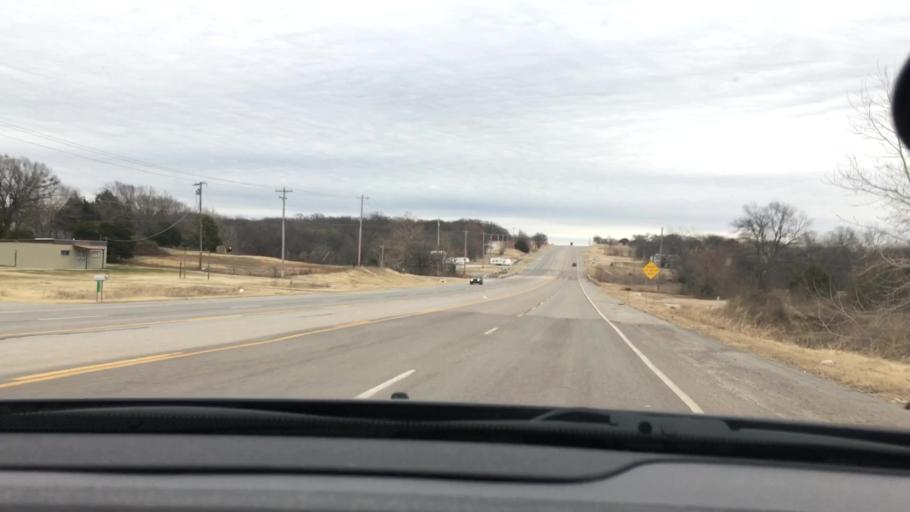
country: US
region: Oklahoma
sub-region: Carter County
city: Dickson
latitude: 34.1871
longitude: -97.0334
